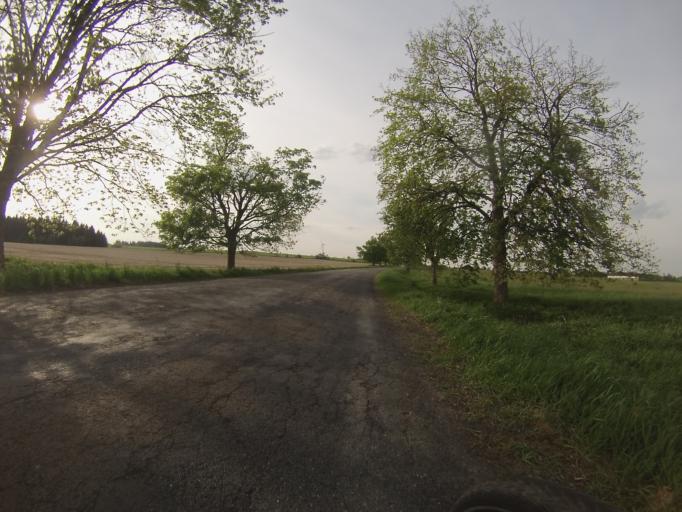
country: CZ
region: Olomoucky
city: Protivanov
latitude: 49.4610
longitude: 16.8695
